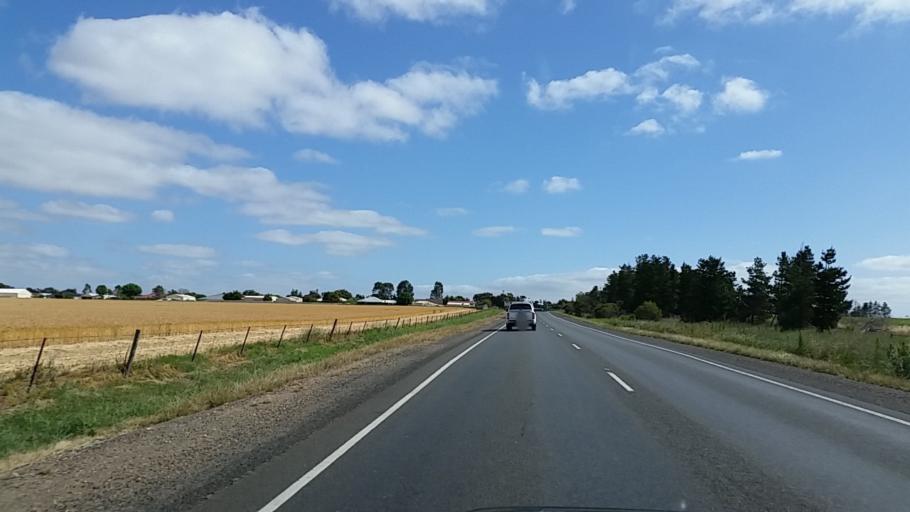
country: AU
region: South Australia
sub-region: Light
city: Roseworthy
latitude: -34.5422
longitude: 138.7495
